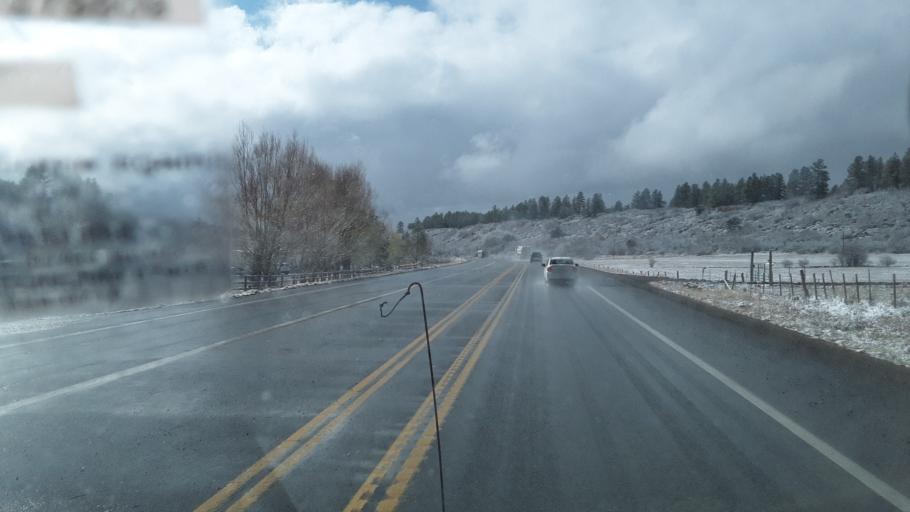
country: US
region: Colorado
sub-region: Archuleta County
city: Pagosa Springs
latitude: 37.2411
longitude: -107.1453
